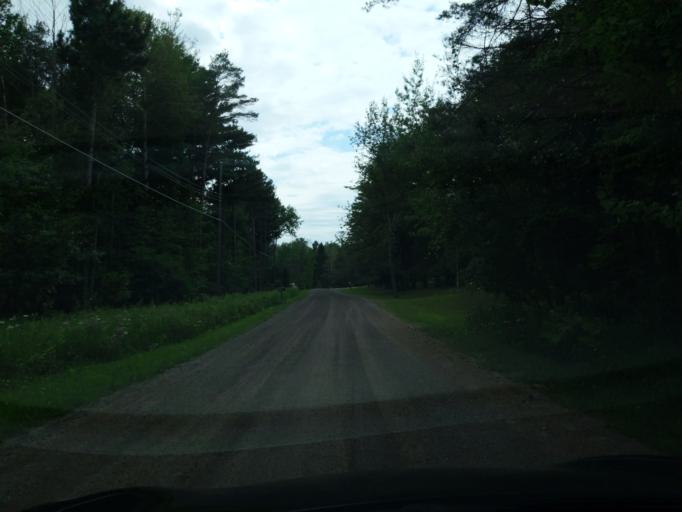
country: US
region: Michigan
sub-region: Clare County
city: Harrison
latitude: 43.9778
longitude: -84.9985
